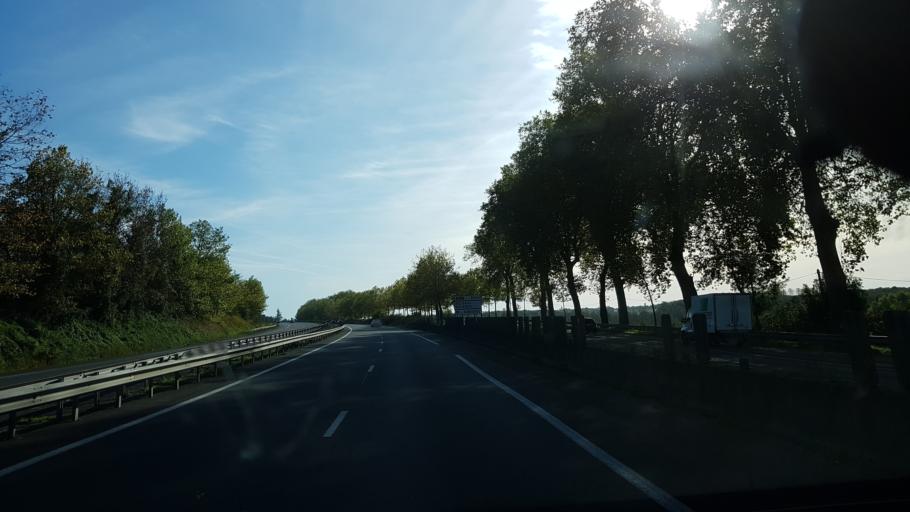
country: FR
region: Poitou-Charentes
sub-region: Departement de la Charente
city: Barbezieux-Saint-Hilaire
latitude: 45.4388
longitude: -0.1730
